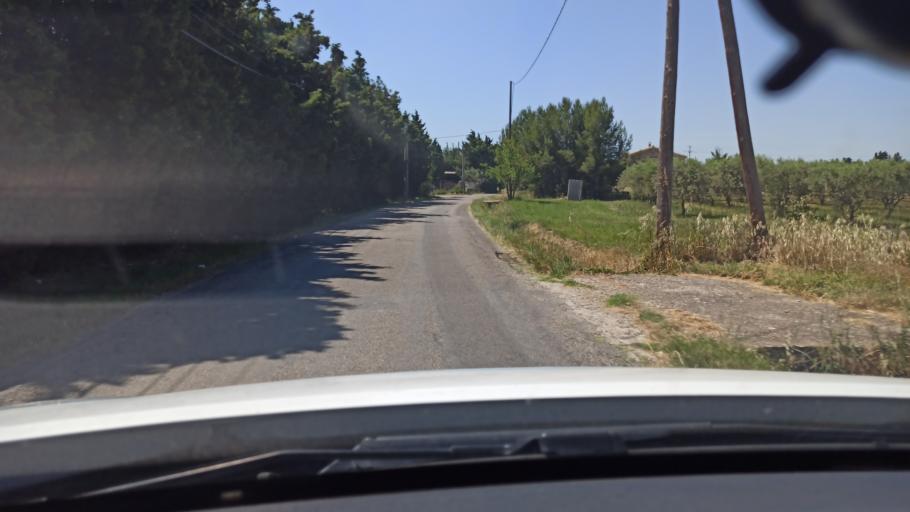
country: FR
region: Provence-Alpes-Cote d'Azur
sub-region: Departement des Bouches-du-Rhone
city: Noves
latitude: 43.8619
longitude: 4.8796
